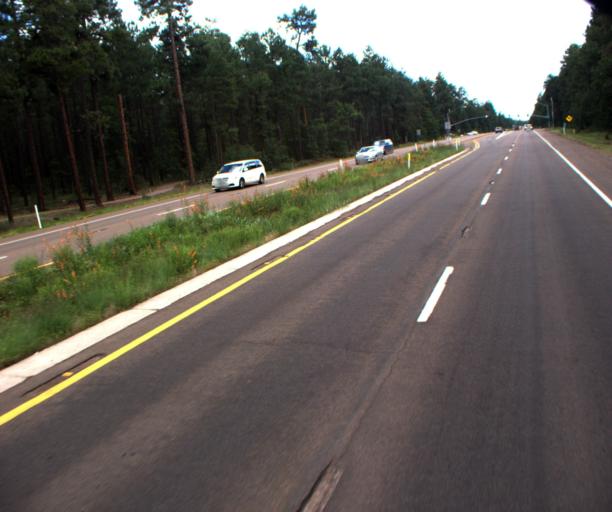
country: US
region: Arizona
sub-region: Navajo County
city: Pinetop-Lakeside
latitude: 34.1175
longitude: -109.9164
